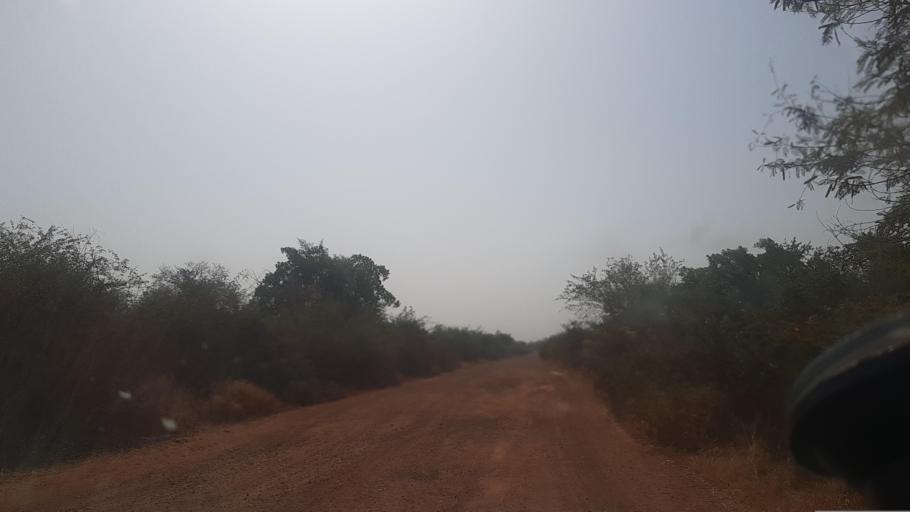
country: ML
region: Segou
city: Baroueli
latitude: 13.0831
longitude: -6.4870
